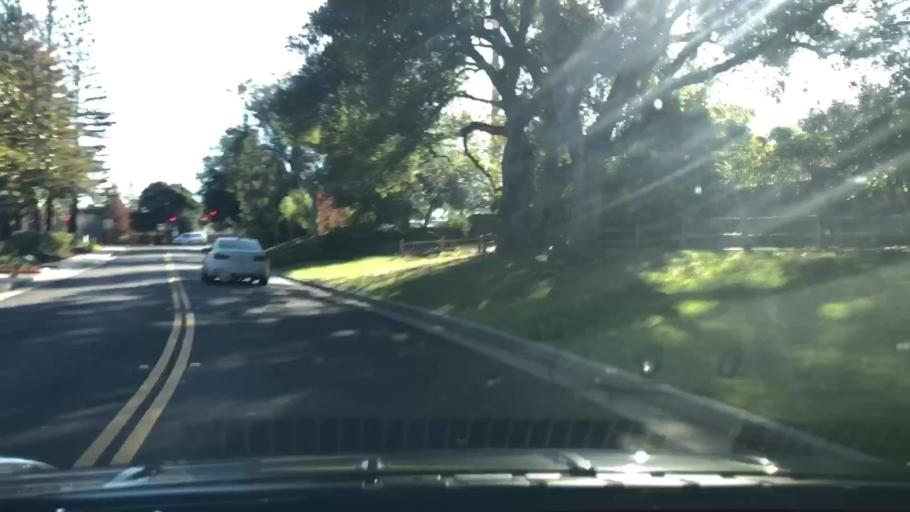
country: US
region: California
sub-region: Santa Clara County
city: Los Gatos
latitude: 37.2549
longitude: -121.9680
